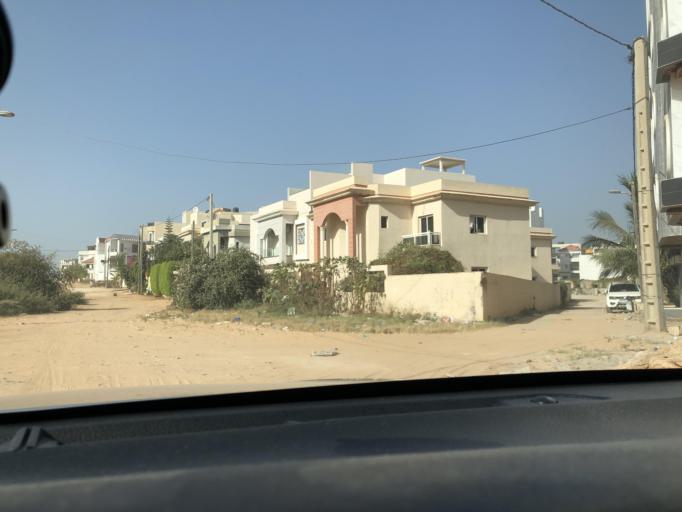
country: SN
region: Dakar
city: Mermoz Boabab
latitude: 14.7338
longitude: -17.5002
